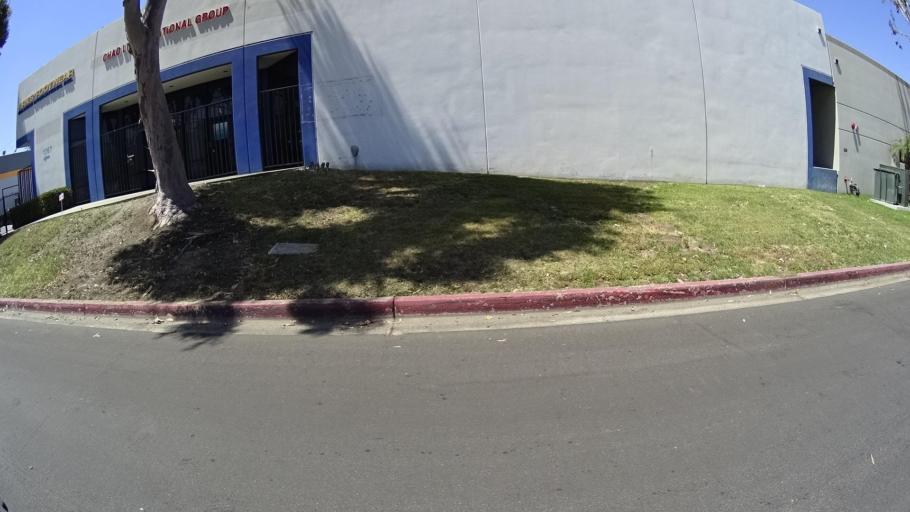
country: US
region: California
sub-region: Los Angeles County
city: La Puente
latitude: 34.0046
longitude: -117.9469
